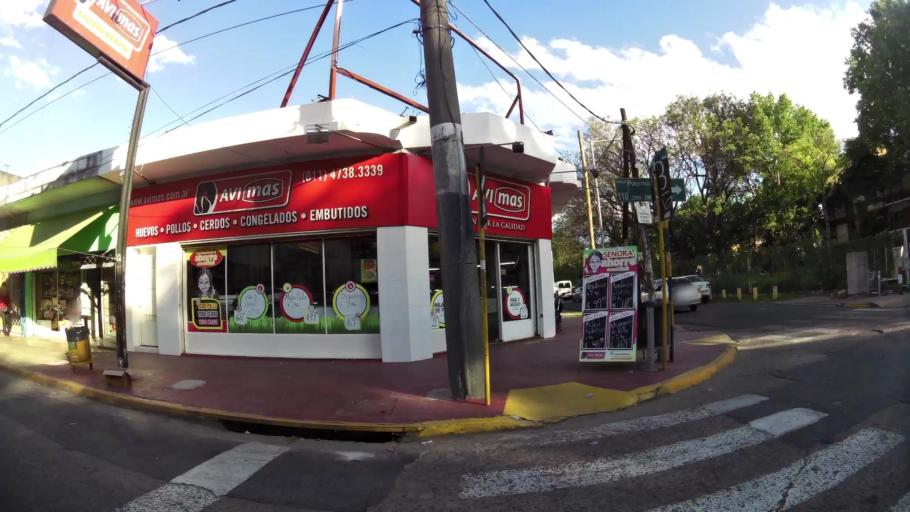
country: AR
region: Buenos Aires
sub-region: Partido de General San Martin
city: General San Martin
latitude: -34.5520
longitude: -58.5544
